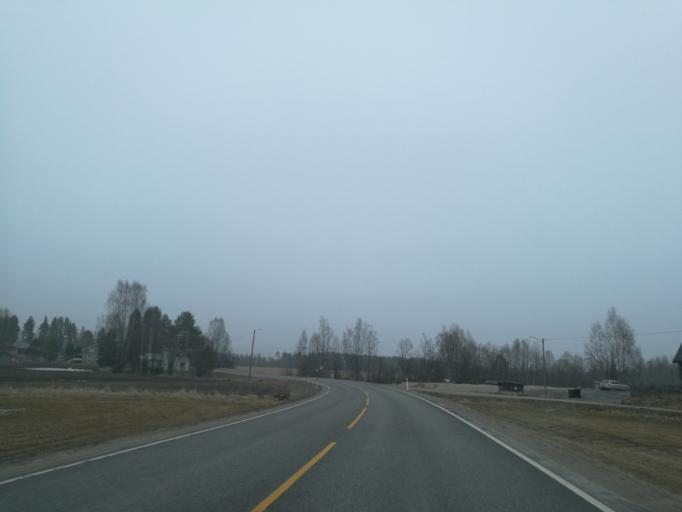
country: NO
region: Hedmark
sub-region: Asnes
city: Flisa
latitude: 60.6638
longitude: 12.0771
